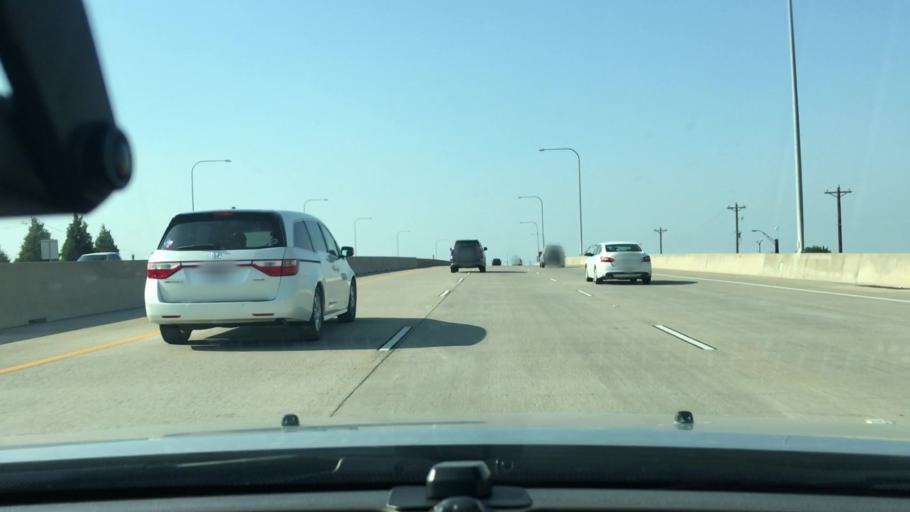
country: US
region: Texas
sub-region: Collin County
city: Frisco
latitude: 33.1885
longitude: -96.8390
